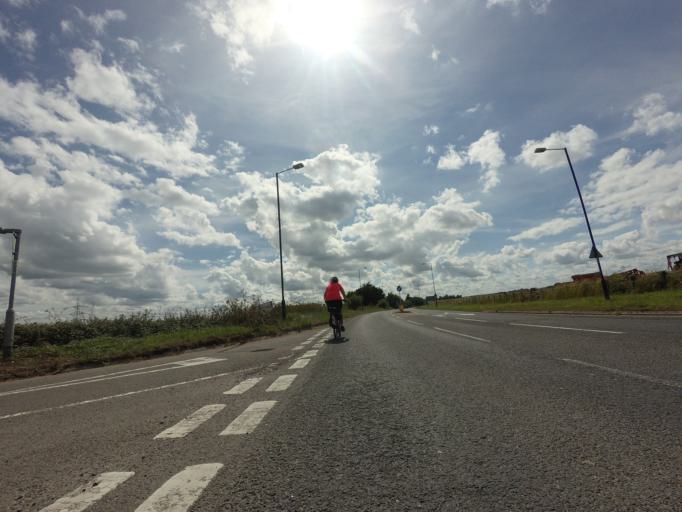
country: GB
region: England
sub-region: Medway
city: Stoke
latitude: 51.4496
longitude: 0.6328
